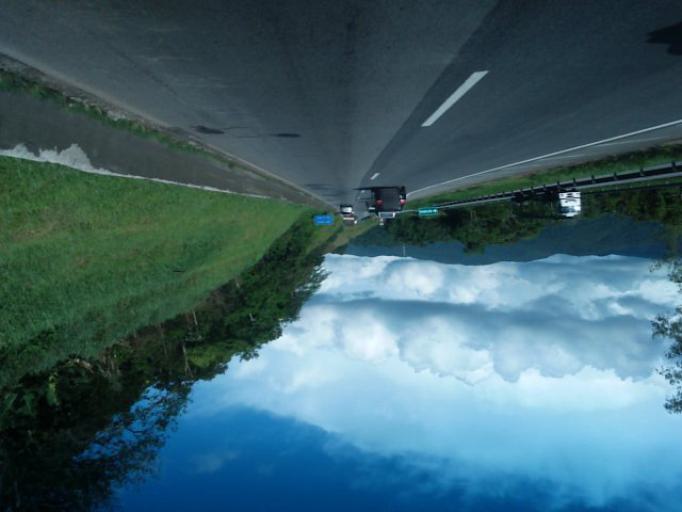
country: BR
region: Sao Paulo
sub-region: Miracatu
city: Miracatu
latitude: -24.1656
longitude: -47.3330
